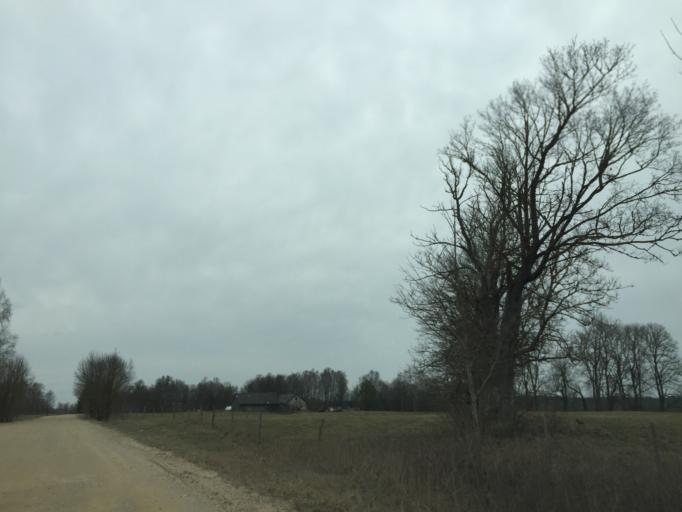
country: LV
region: Livani
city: Livani
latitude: 56.2968
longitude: 26.1727
